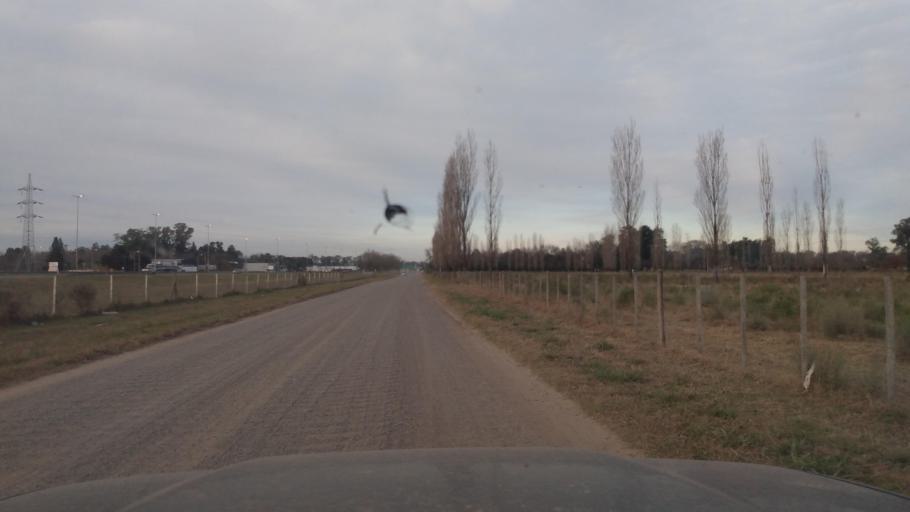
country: AR
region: Buenos Aires
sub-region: Partido de Lujan
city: Lujan
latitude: -34.5750
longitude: -59.0757
